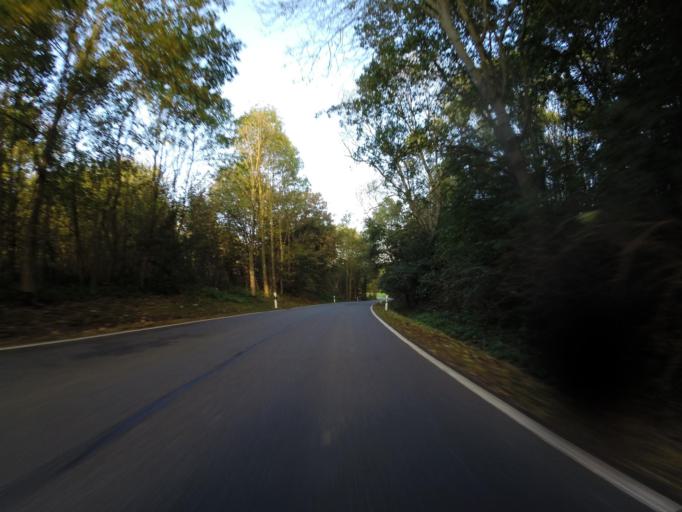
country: DE
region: Thuringia
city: Grossschwabhausen
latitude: 50.9615
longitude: 11.5281
